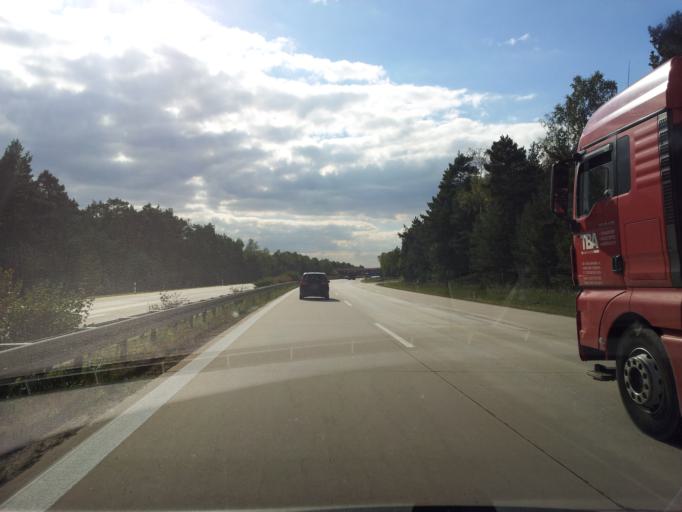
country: DE
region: Brandenburg
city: Schipkau
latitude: 51.4934
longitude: 13.8958
